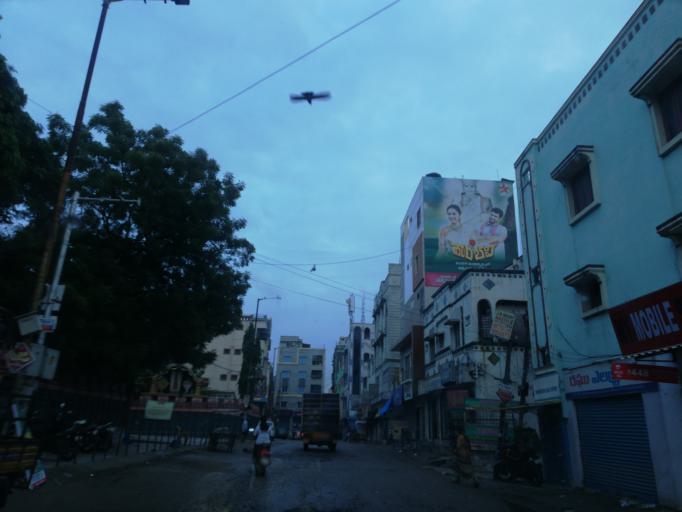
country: IN
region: Telangana
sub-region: Rangareddi
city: Kukatpalli
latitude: 17.4880
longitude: 78.3958
